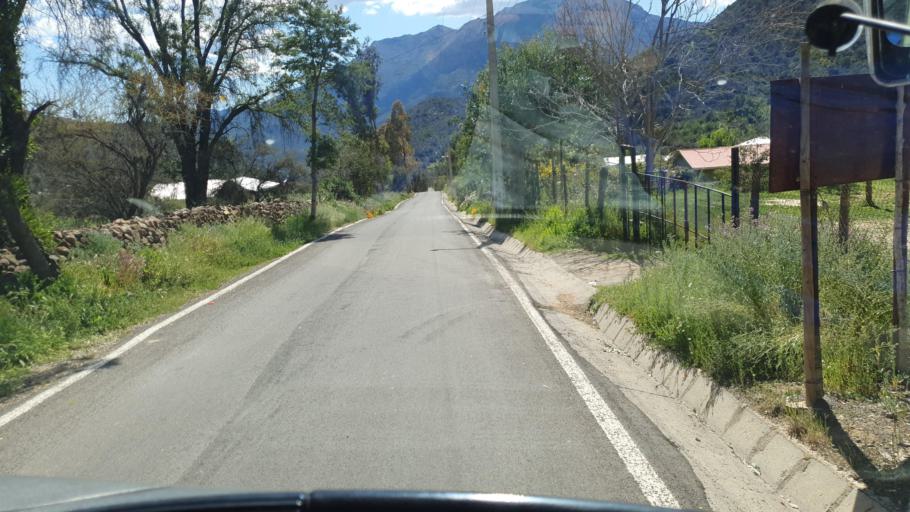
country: CL
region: Santiago Metropolitan
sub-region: Provincia de Chacabuco
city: Lampa
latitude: -33.1911
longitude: -71.0978
